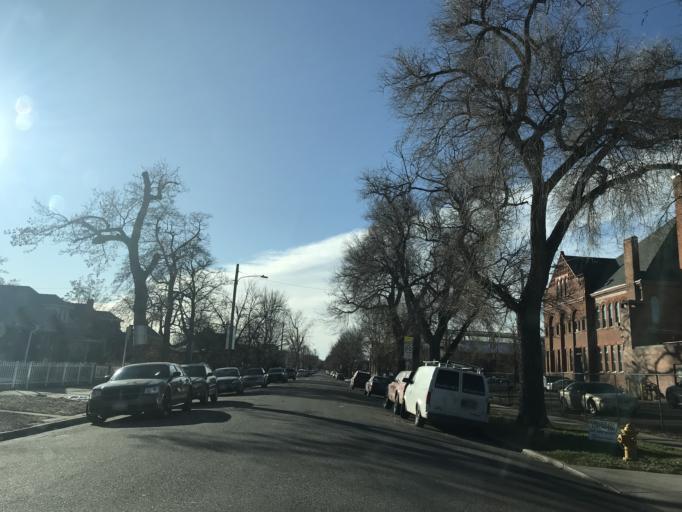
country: US
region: Colorado
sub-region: Denver County
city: Denver
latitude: 39.7680
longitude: -104.9672
